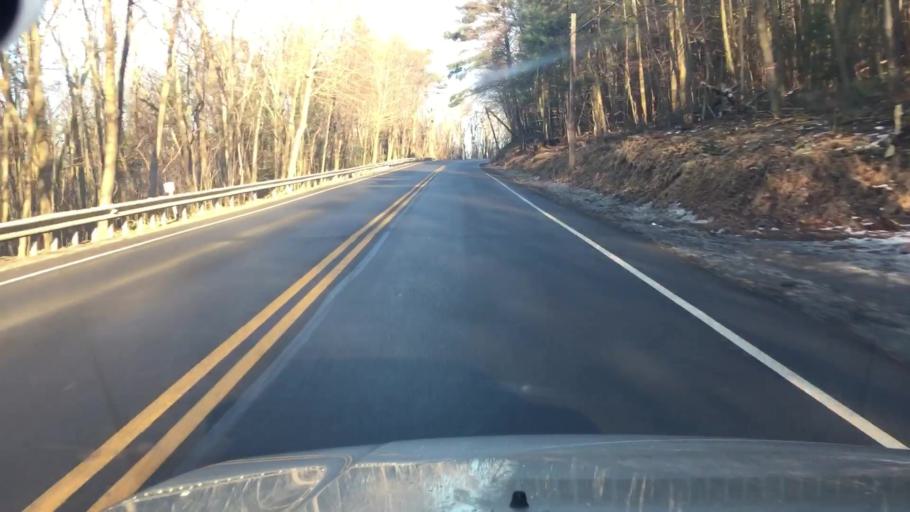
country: US
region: Pennsylvania
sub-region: Luzerne County
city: Conyngham
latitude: 41.0328
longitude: -76.1211
